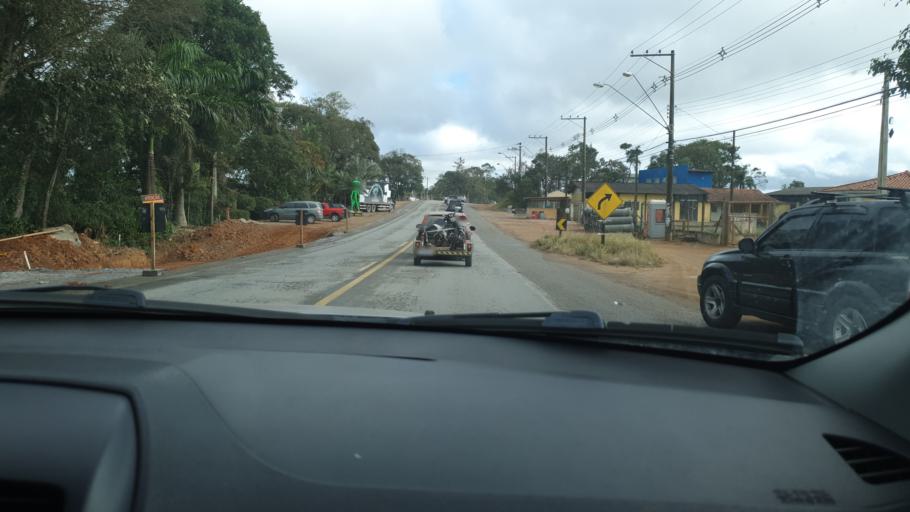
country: BR
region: Sao Paulo
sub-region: Ibiuna
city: Ibiuna
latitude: -23.6611
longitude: -47.1955
